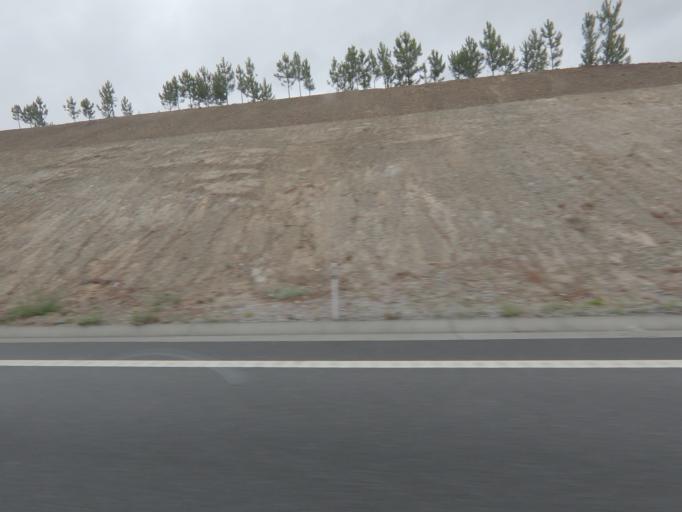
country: PT
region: Vila Real
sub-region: Vila Real
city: Vila Real
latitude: 41.2674
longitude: -7.7870
